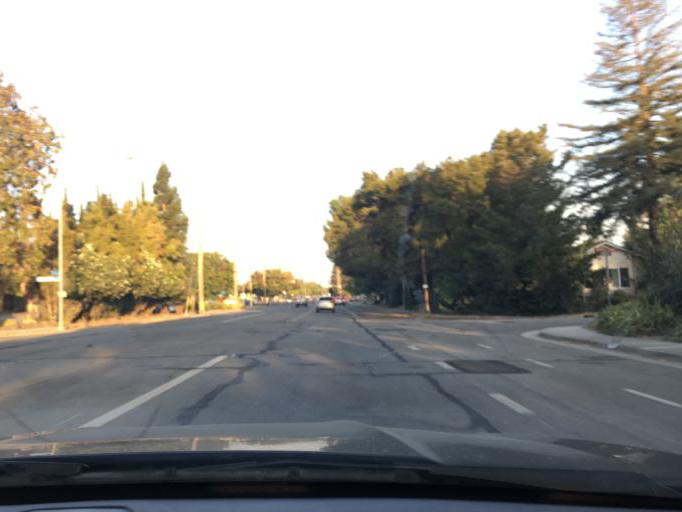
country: US
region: California
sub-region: Santa Clara County
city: Cupertino
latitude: 37.2938
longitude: -122.0346
